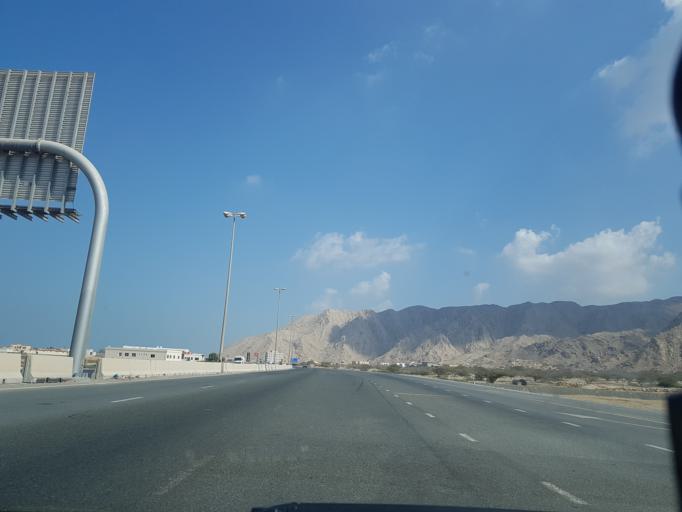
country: AE
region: Ra's al Khaymah
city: Ras al-Khaimah
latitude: 25.8419
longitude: 56.0182
